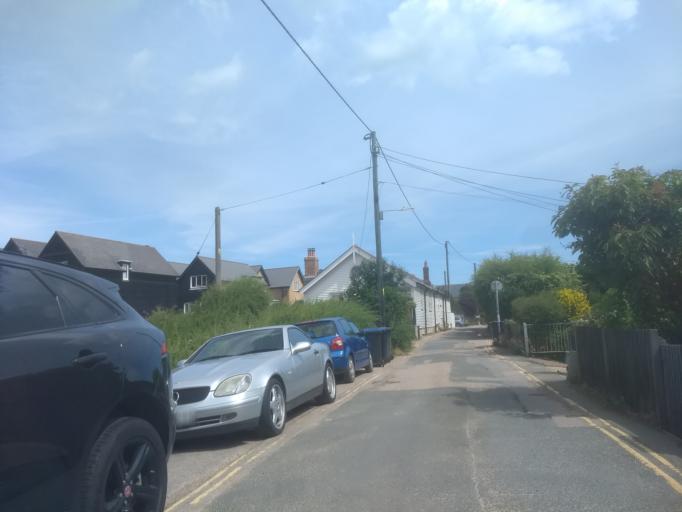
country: GB
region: England
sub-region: Kent
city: Whitstable
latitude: 51.3556
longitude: 1.0176
